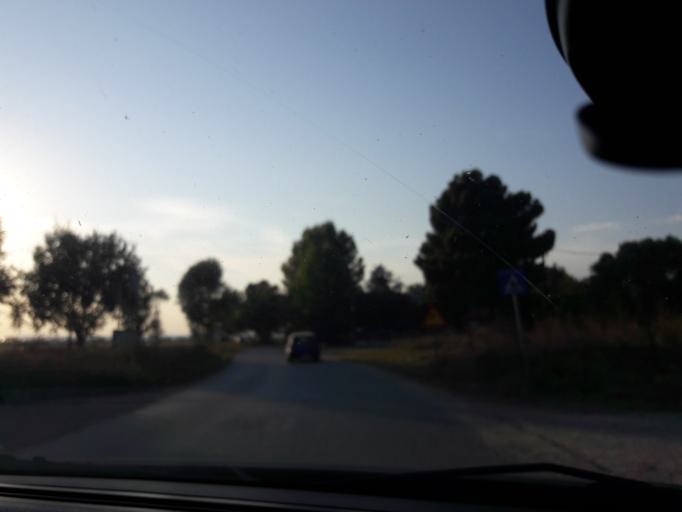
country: GR
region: Central Macedonia
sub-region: Nomos Chalkidikis
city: Nea Kallikrateia
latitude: 40.3355
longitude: 23.0218
